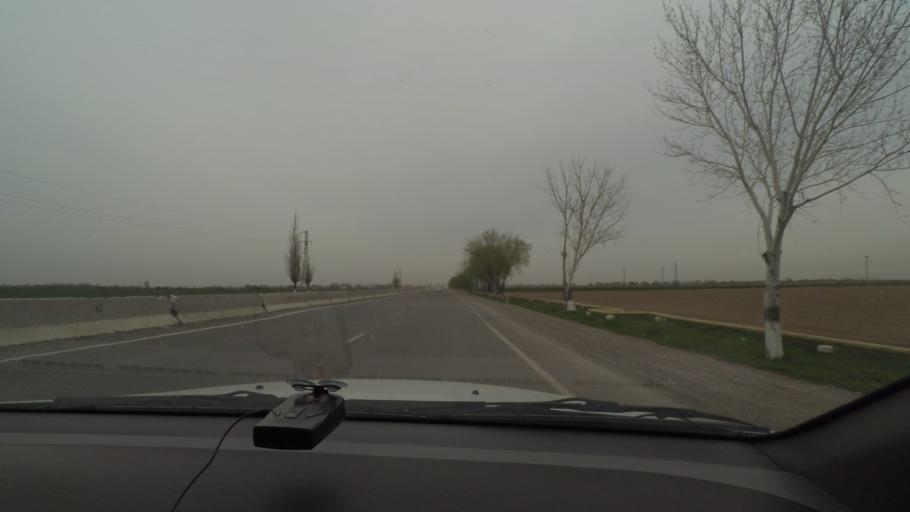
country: KZ
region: Ongtustik Qazaqstan
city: Myrzakent
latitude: 40.5570
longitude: 68.3897
